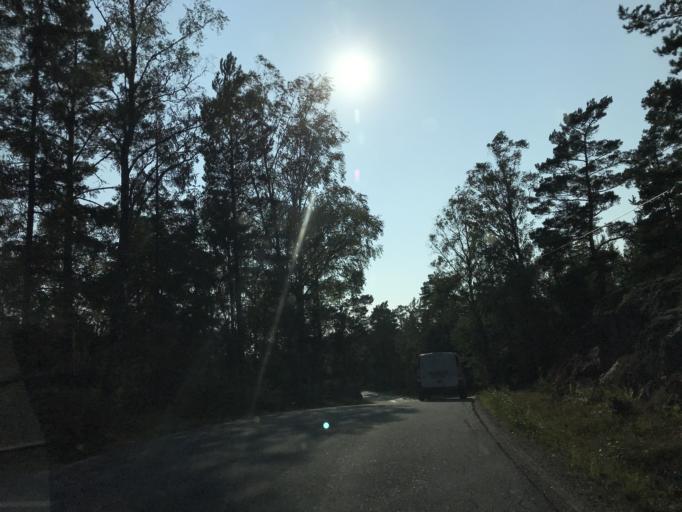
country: SE
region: Stockholm
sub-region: Norrtalje Kommun
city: Bjorko
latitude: 59.8644
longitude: 19.0463
